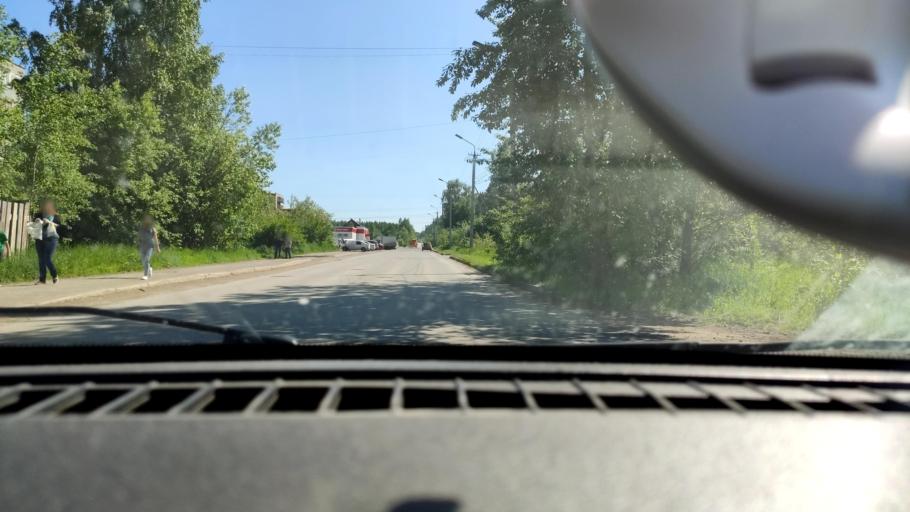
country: RU
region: Perm
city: Polazna
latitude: 58.1471
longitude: 56.4327
